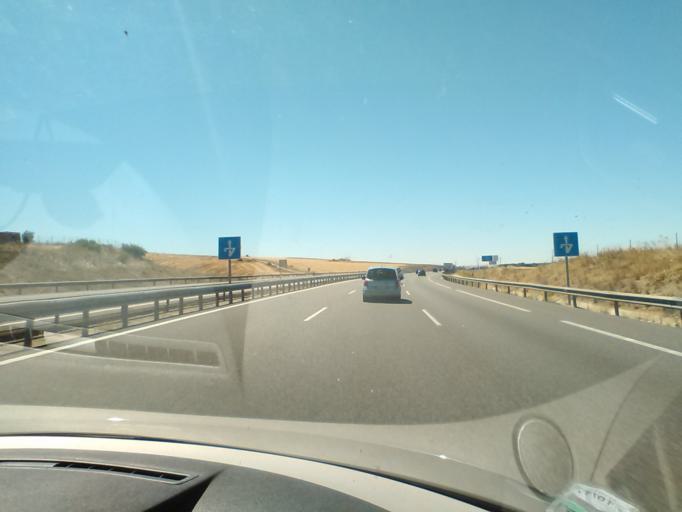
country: ES
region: Castille and Leon
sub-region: Provincia de Burgos
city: Cardenadijo
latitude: 42.3254
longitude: -3.6636
